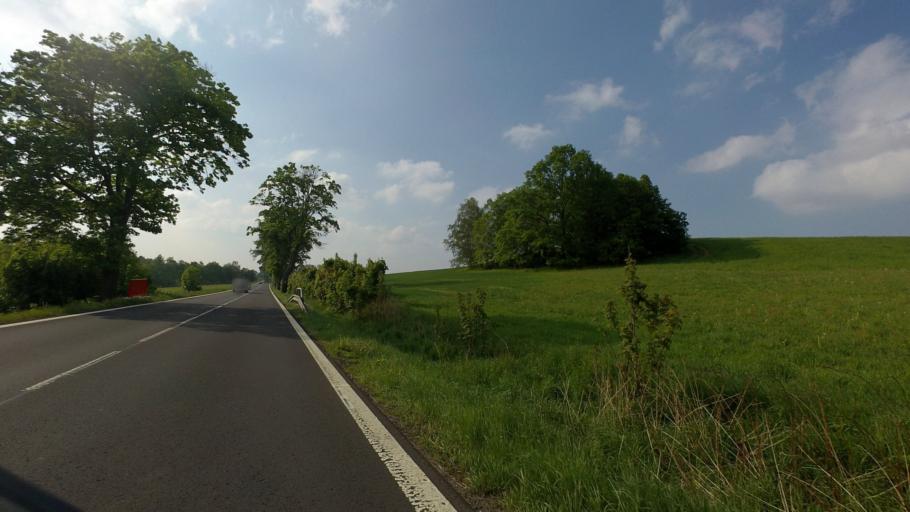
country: CZ
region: Ustecky
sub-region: Okres Decin
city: Sluknov
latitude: 50.9956
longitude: 14.4793
